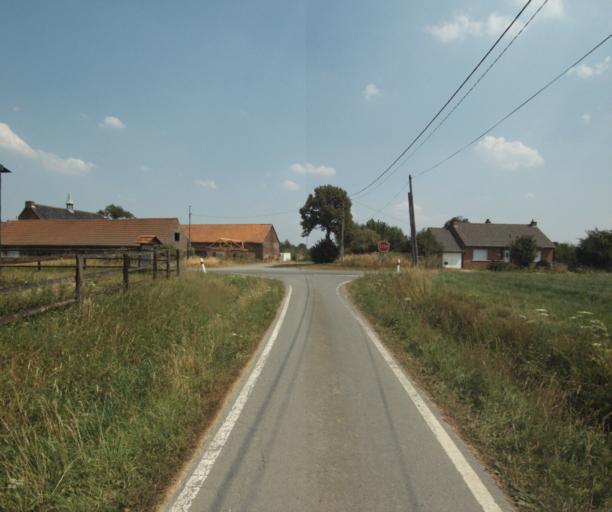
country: FR
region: Nord-Pas-de-Calais
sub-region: Departement du Nord
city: Quesnoy-sur-Deule
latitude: 50.7250
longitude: 3.0203
